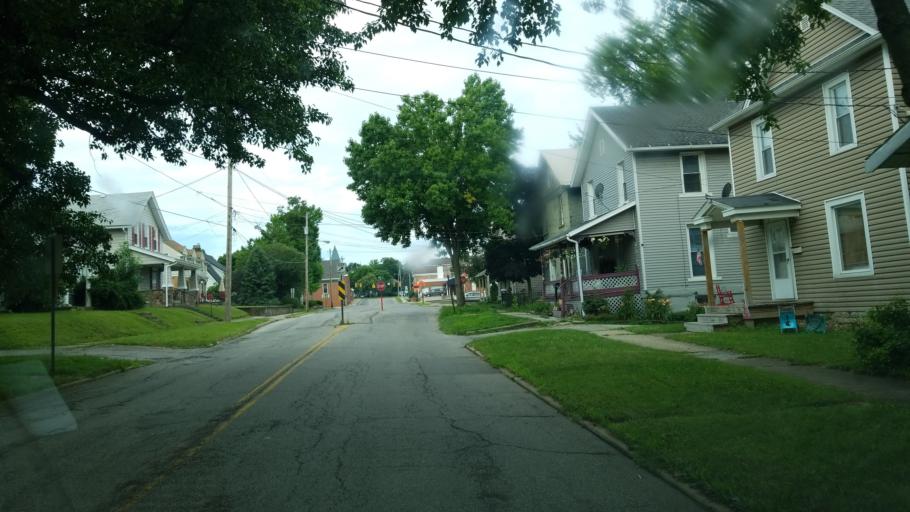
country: US
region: Ohio
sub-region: Ashland County
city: Ashland
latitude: 40.8671
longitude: -82.3116
